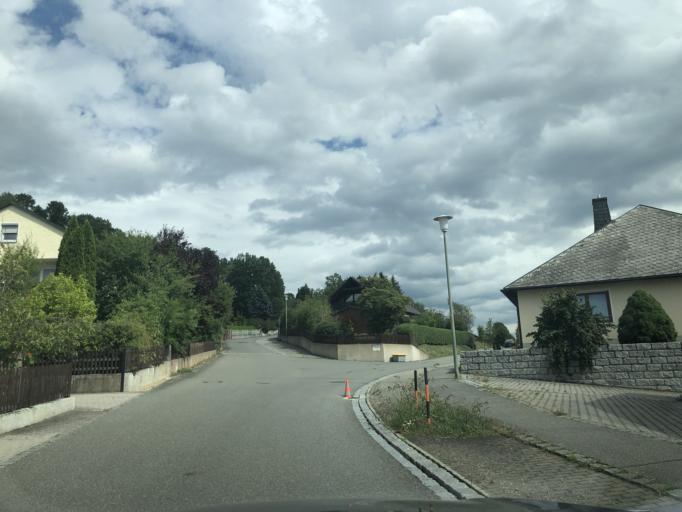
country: DE
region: Bavaria
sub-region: Upper Palatinate
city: Pressath
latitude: 49.7714
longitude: 11.9410
